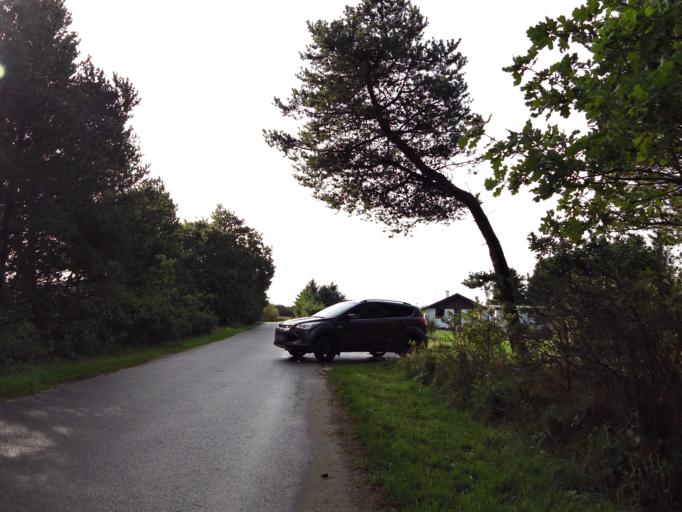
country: DK
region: South Denmark
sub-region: Varde Kommune
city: Oksbol
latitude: 55.5566
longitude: 8.2229
